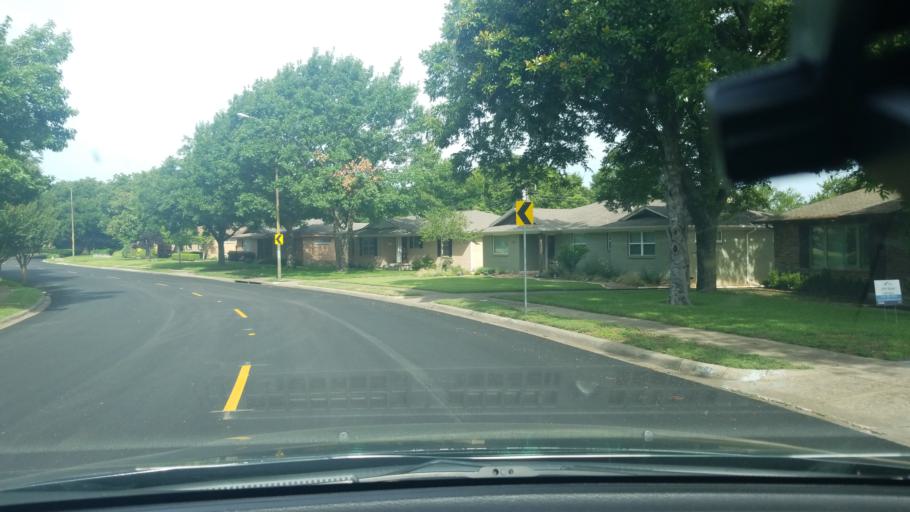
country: US
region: Texas
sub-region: Dallas County
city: Highland Park
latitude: 32.8075
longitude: -96.7024
